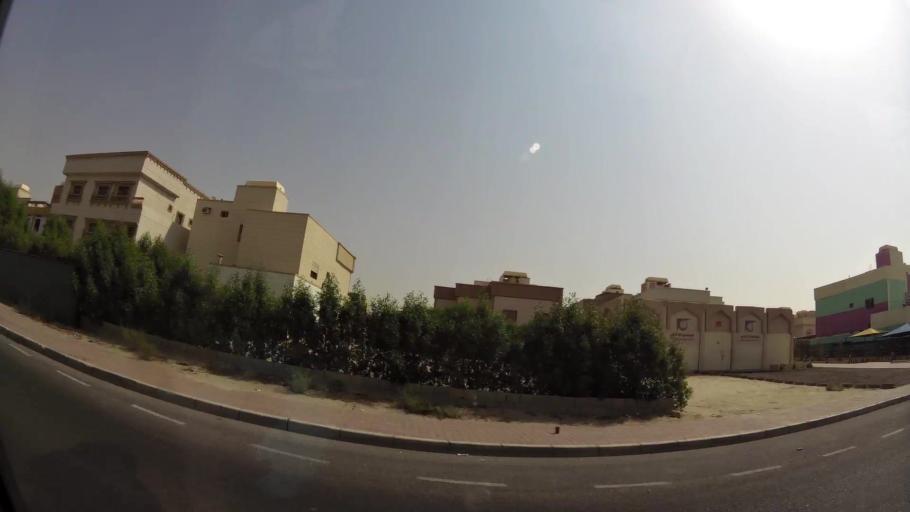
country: KW
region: Muhafazat al Jahra'
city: Al Jahra'
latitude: 29.3186
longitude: 47.7121
